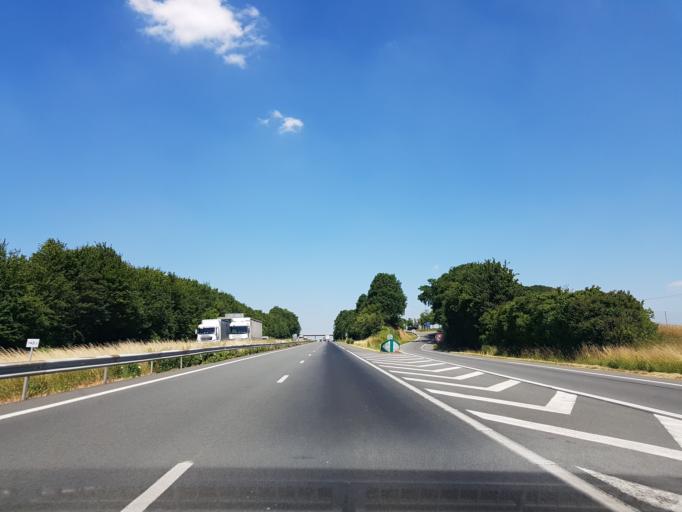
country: FR
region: Nord-Pas-de-Calais
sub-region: Departement du Nord
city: Marcoing
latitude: 50.0882
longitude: 3.1717
